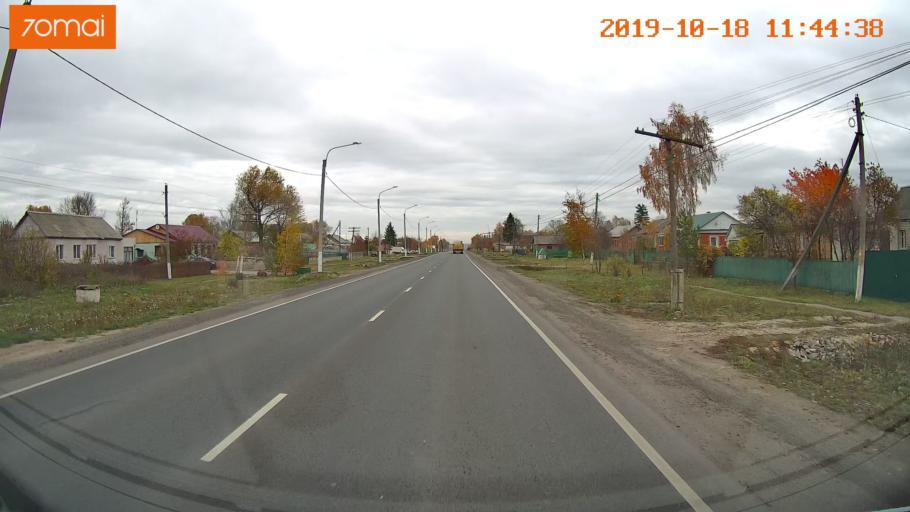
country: RU
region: Rjazan
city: Oktyabr'skiy
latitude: 54.2038
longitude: 38.9603
